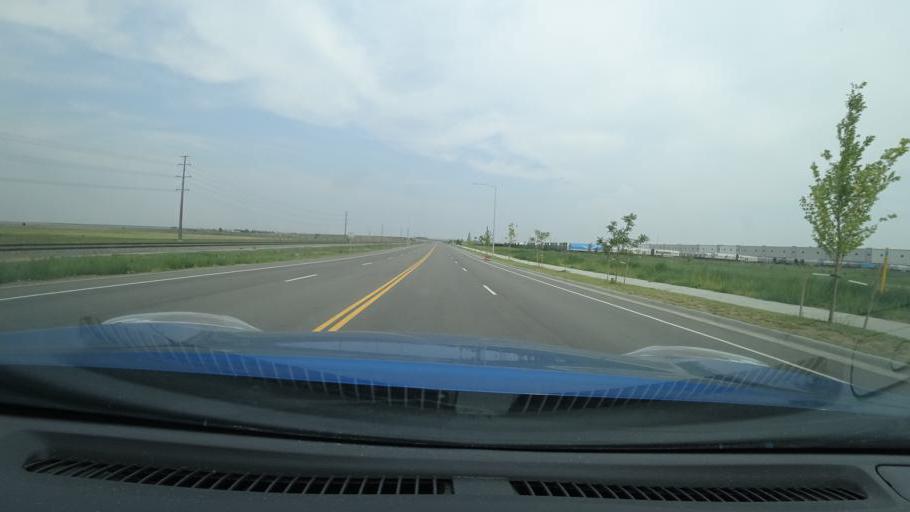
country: US
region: Colorado
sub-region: Adams County
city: Aurora
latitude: 39.7496
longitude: -104.7278
